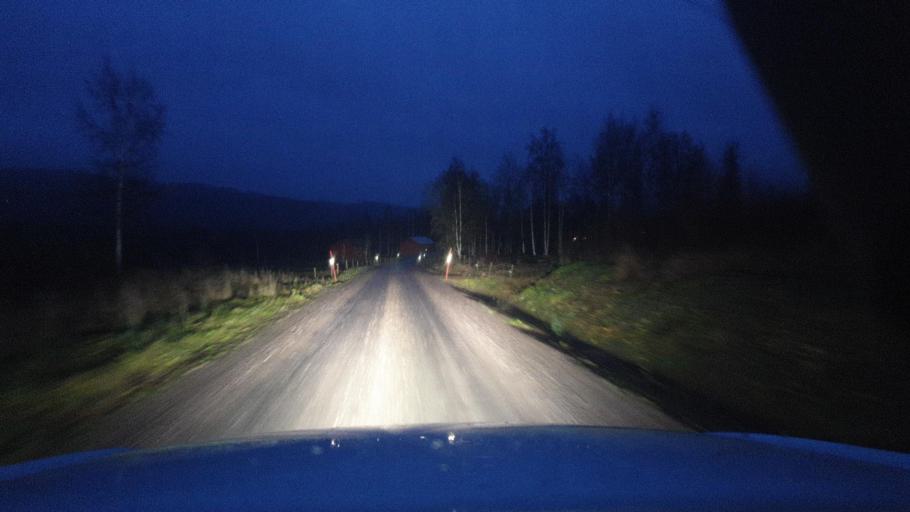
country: SE
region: Vaermland
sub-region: Torsby Kommun
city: Torsby
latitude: 59.9569
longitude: 12.8895
